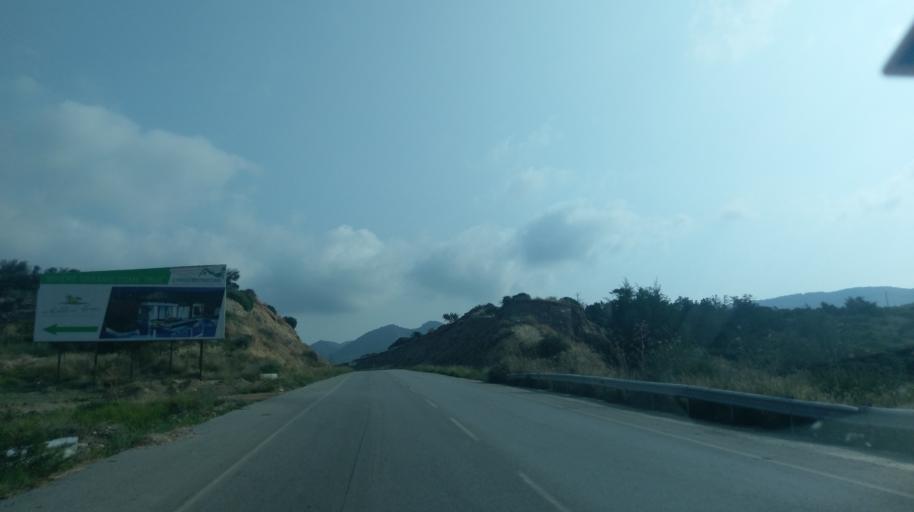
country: CY
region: Ammochostos
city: Lefkonoiko
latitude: 35.3531
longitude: 33.6224
